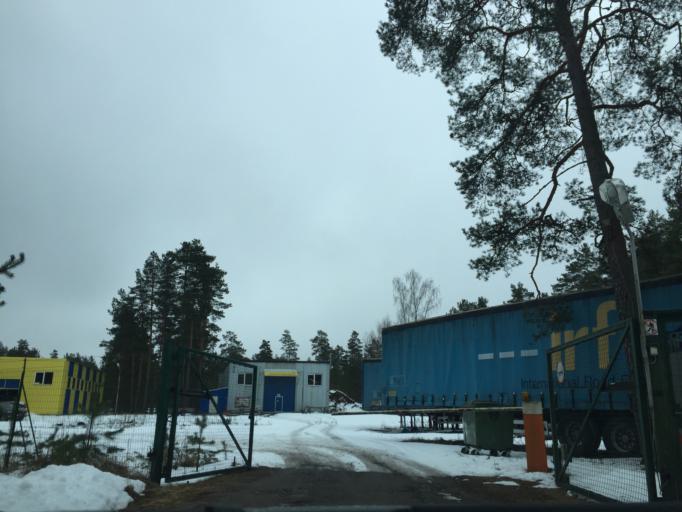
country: LV
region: Garkalne
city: Garkalne
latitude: 57.0414
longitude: 24.4324
